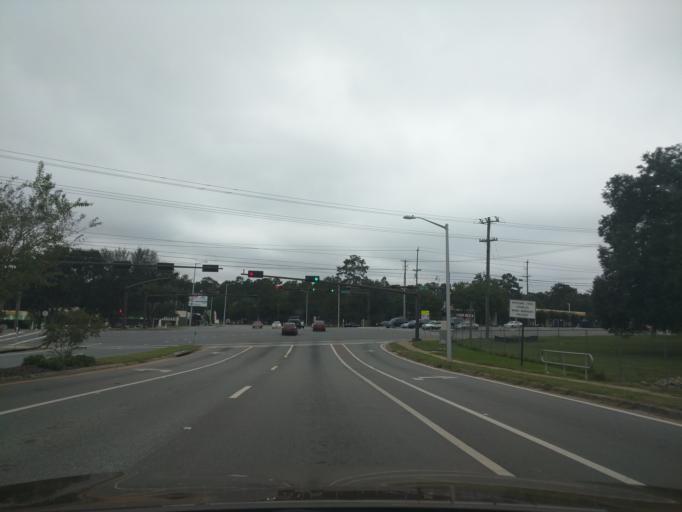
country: US
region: Florida
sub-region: Leon County
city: Tallahassee
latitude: 30.4411
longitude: -84.2259
